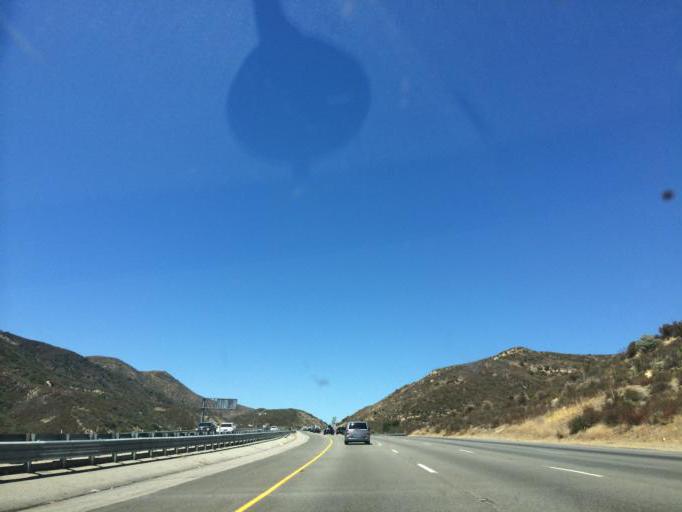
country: US
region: California
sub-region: Los Angeles County
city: Castaic
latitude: 34.5801
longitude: -118.7031
